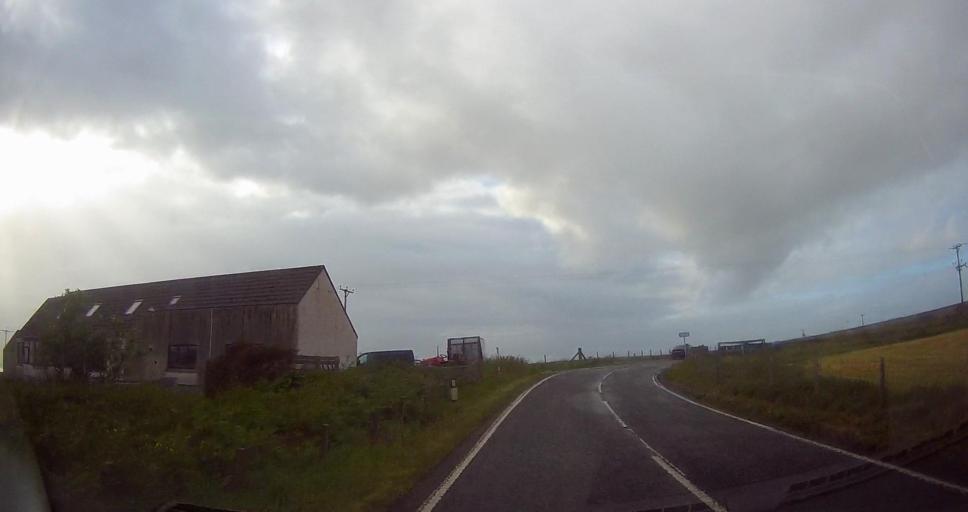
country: GB
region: Scotland
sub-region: Orkney Islands
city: Stromness
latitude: 58.9375
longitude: -3.2132
